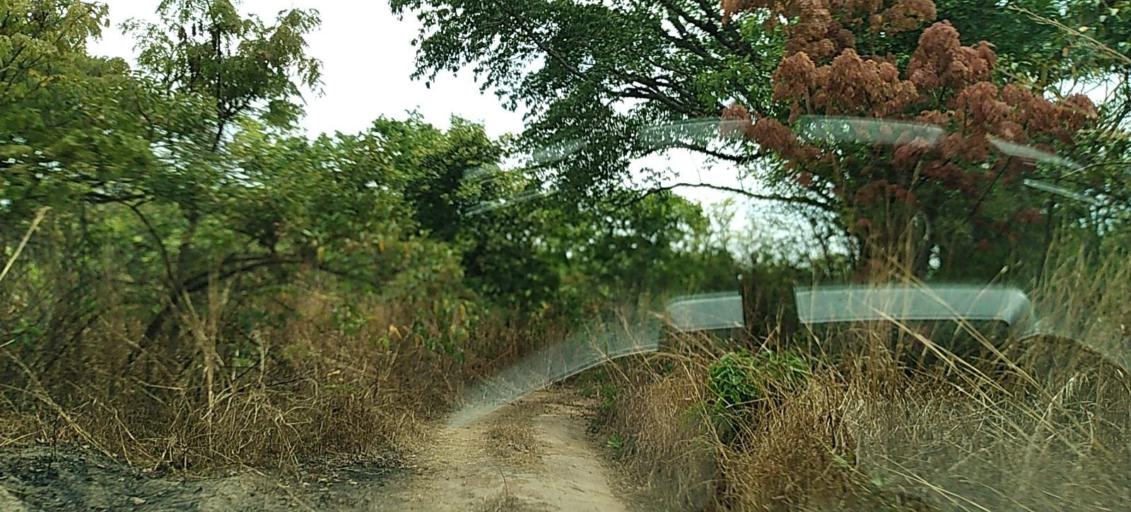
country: ZM
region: Copperbelt
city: Chililabombwe
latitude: -12.3291
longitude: 27.7701
